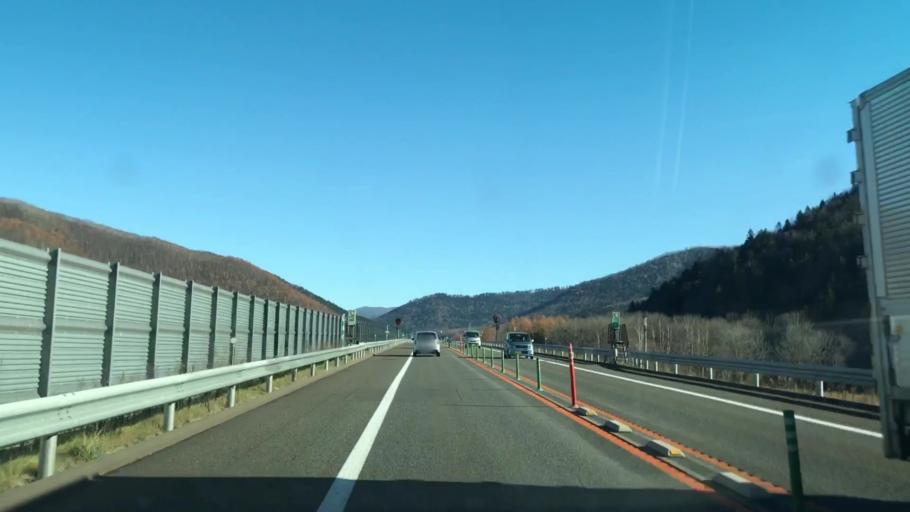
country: JP
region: Hokkaido
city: Shimo-furano
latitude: 43.0641
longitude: 142.5436
